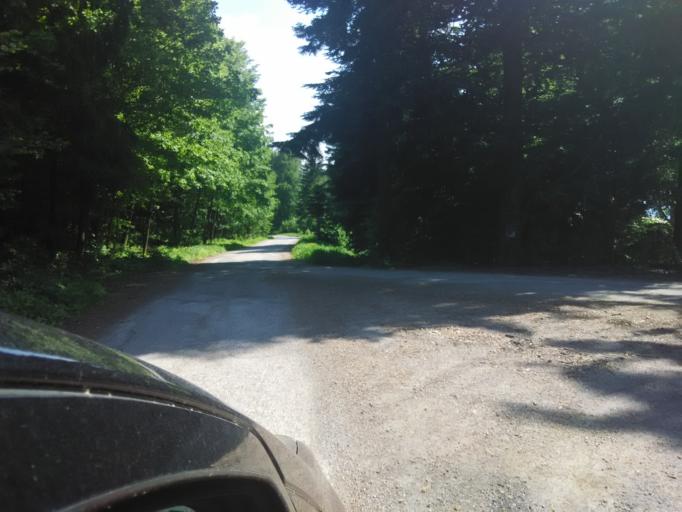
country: SK
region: Kosicky
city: Dobsina
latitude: 48.6590
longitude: 20.2955
